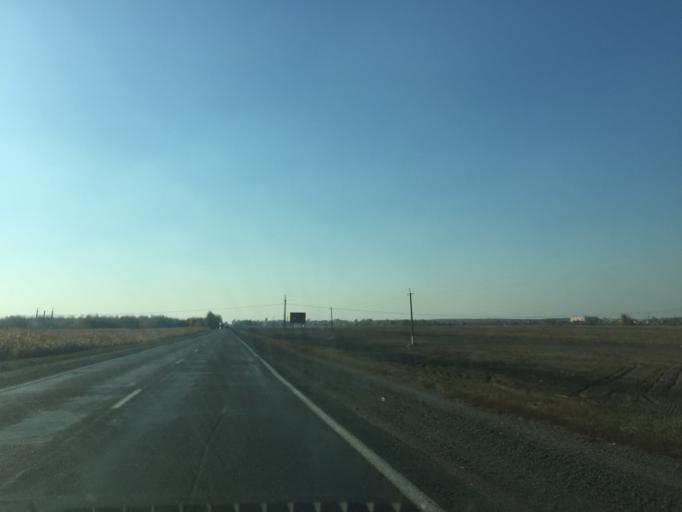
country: BY
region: Gomel
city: Dobrush
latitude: 52.3842
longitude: 31.3776
